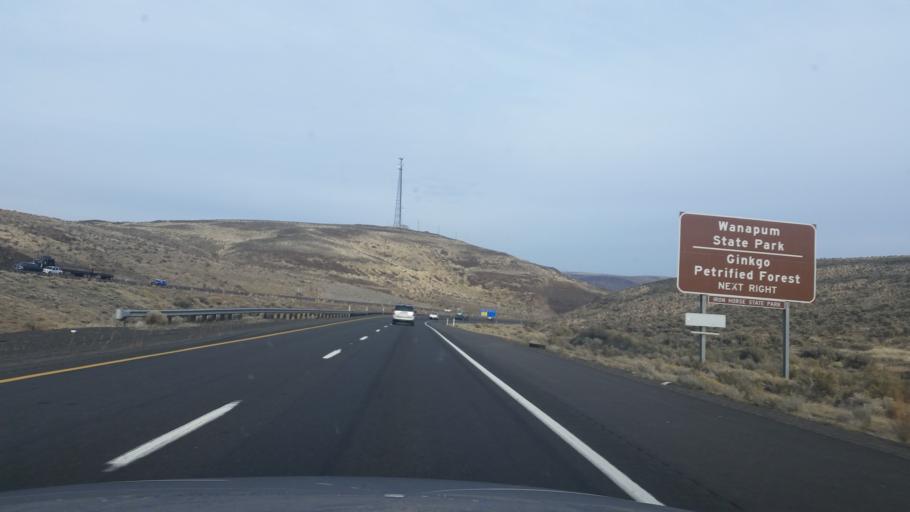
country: US
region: Washington
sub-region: Grant County
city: Mattawa
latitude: 46.9394
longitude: -120.0080
